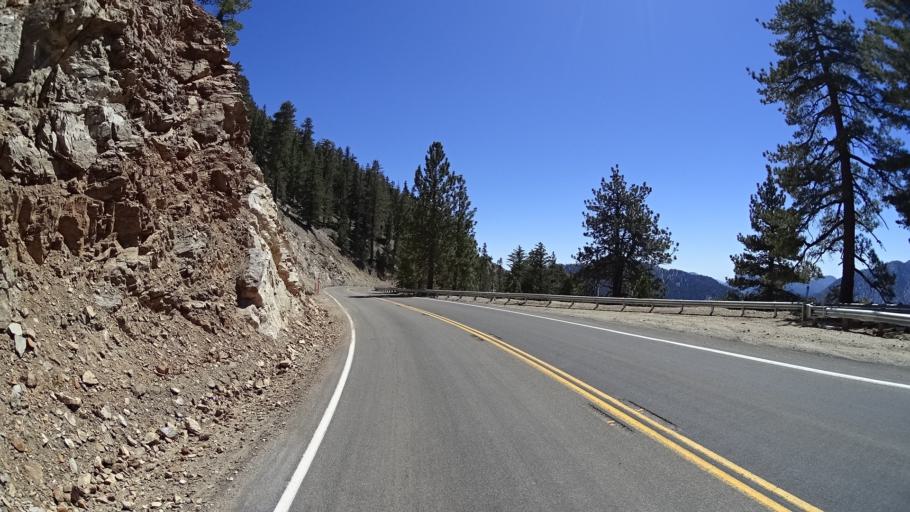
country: US
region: California
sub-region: San Bernardino County
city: Wrightwood
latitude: 34.3648
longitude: -117.8069
